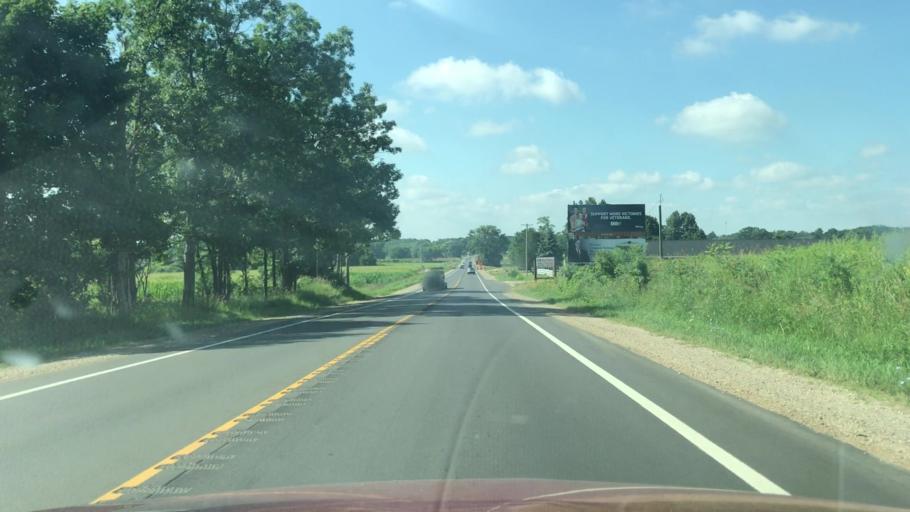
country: US
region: Michigan
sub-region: Newaygo County
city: Newaygo
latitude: 43.3702
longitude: -85.8009
